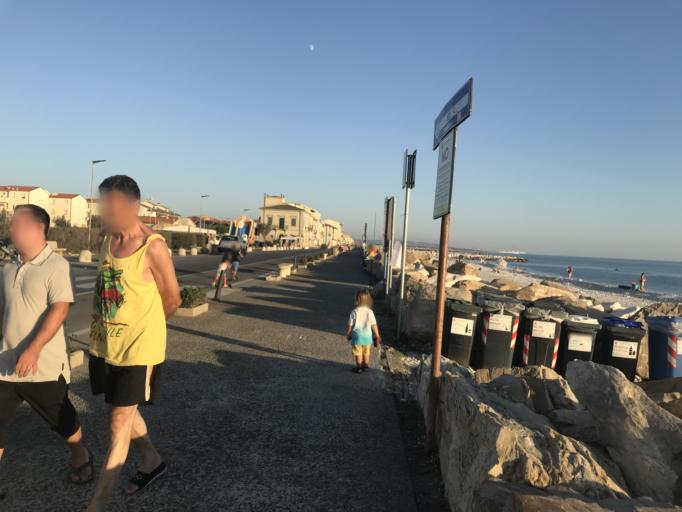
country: IT
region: Tuscany
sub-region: Province of Pisa
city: Marina di Pisa
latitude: 43.6683
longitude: 10.2746
